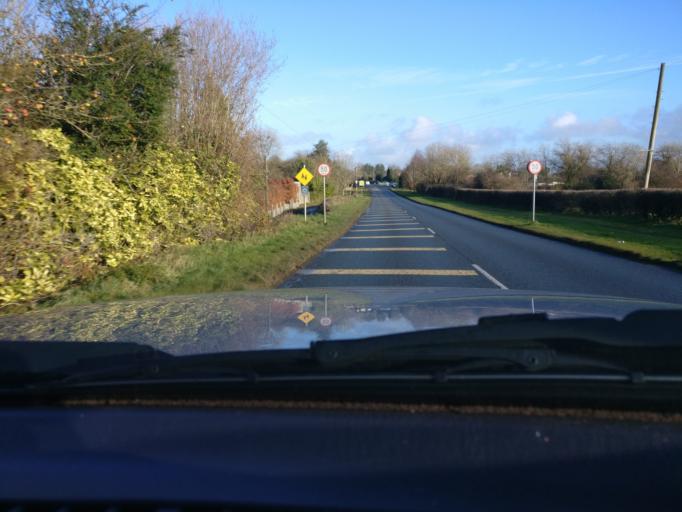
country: IE
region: Leinster
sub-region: An Iarmhi
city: An Muileann gCearr
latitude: 53.5116
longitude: -7.4013
